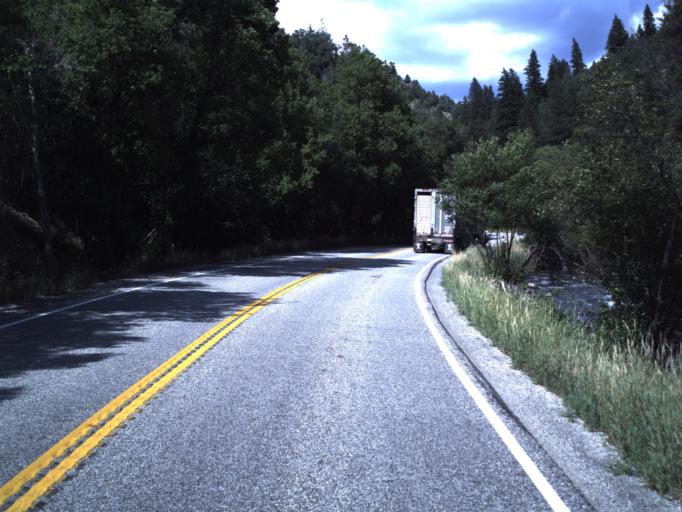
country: US
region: Utah
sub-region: Cache County
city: North Logan
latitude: 41.8100
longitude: -111.6263
